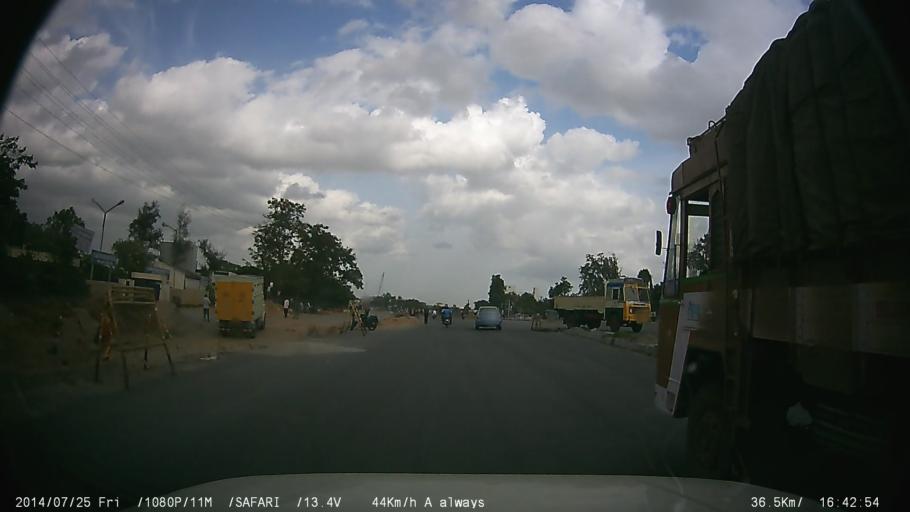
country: IN
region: Tamil Nadu
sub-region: Krishnagiri
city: Hosur
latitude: 12.7505
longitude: 77.8054
